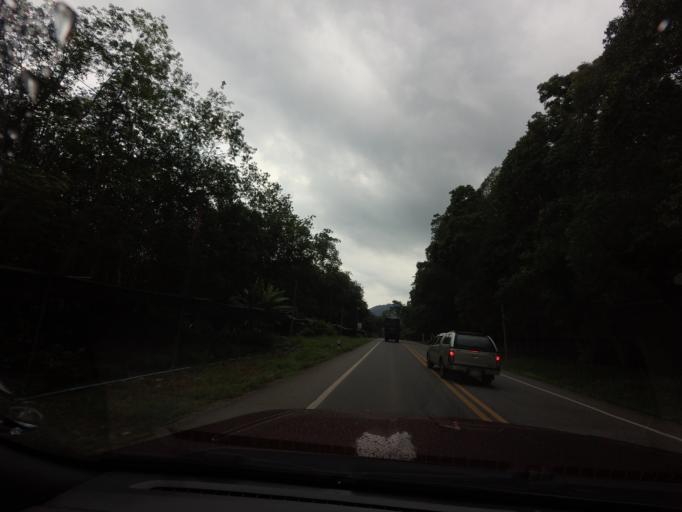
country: TH
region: Yala
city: Ban Nang Sata
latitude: 6.2372
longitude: 101.2170
